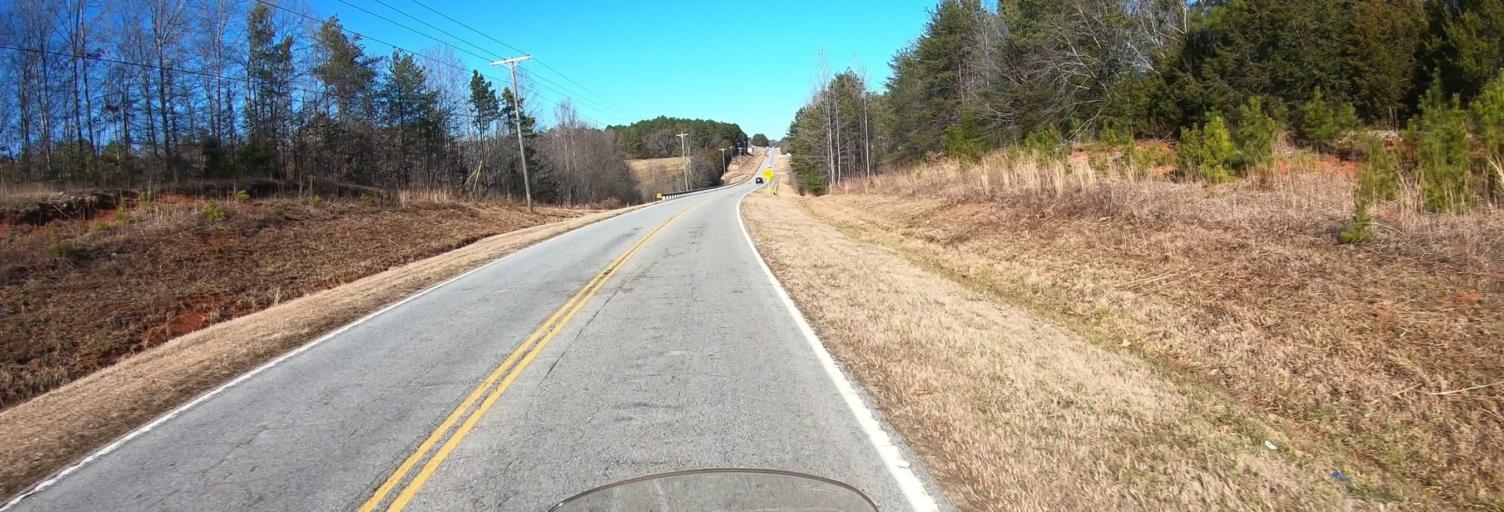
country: US
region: South Carolina
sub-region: Oconee County
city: Walhalla
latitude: 34.7330
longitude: -83.0564
